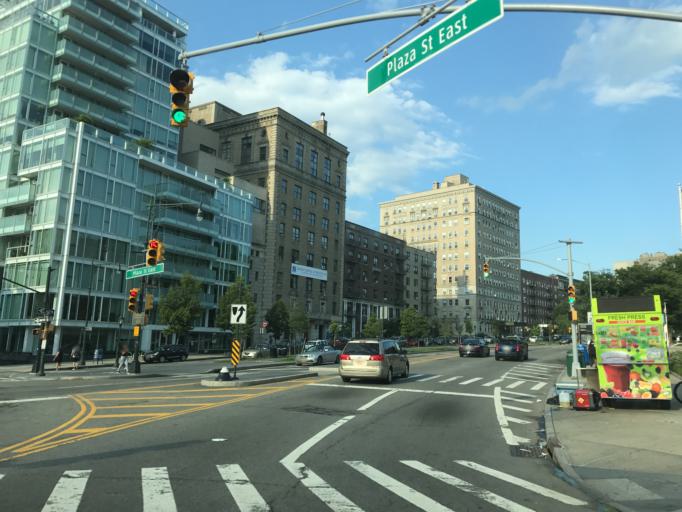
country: US
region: New York
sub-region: Kings County
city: Brooklyn
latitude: 40.6728
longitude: -73.9690
